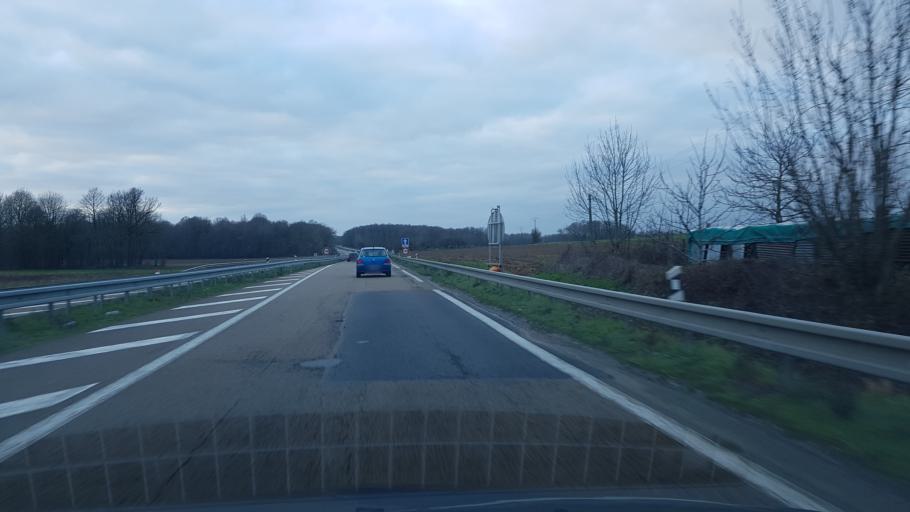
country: FR
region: Champagne-Ardenne
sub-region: Departement de la Marne
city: Esternay
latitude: 48.7323
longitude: 3.6050
